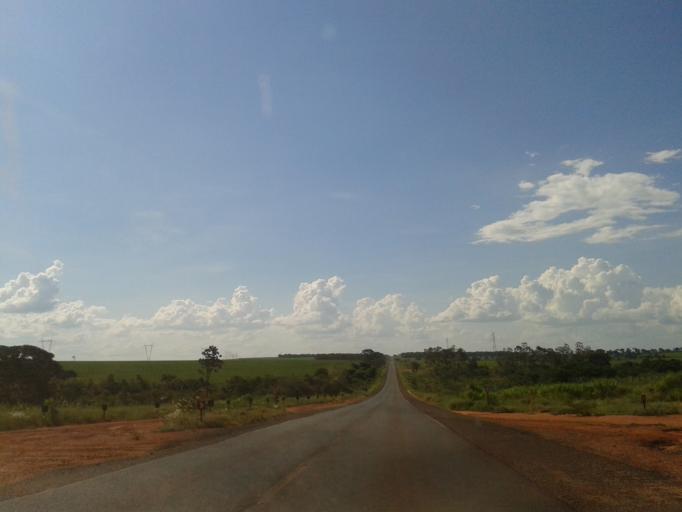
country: BR
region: Minas Gerais
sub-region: Santa Vitoria
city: Santa Vitoria
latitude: -19.0661
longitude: -50.3791
